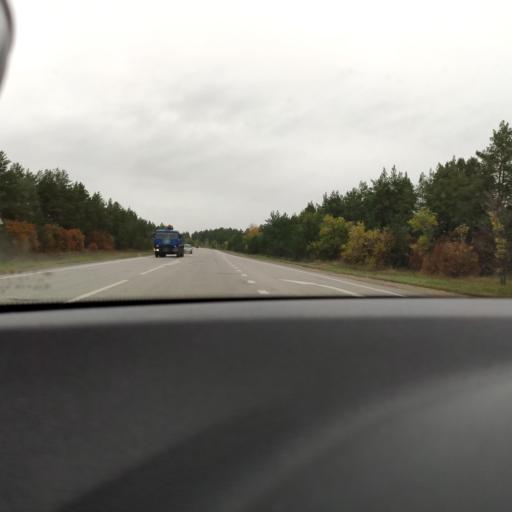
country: RU
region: Samara
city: Mirnyy
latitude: 53.5338
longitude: 50.3032
